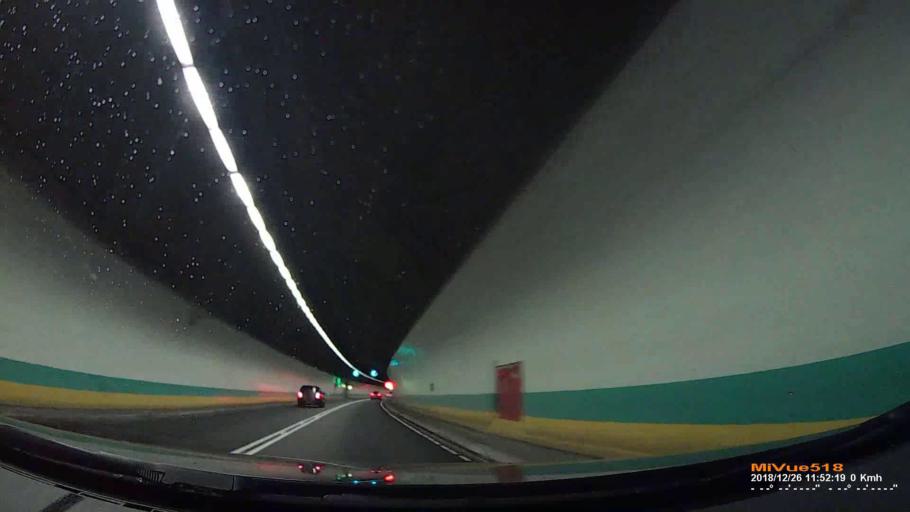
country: TW
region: Taiwan
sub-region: Keelung
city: Keelung
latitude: 24.9674
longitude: 121.6841
